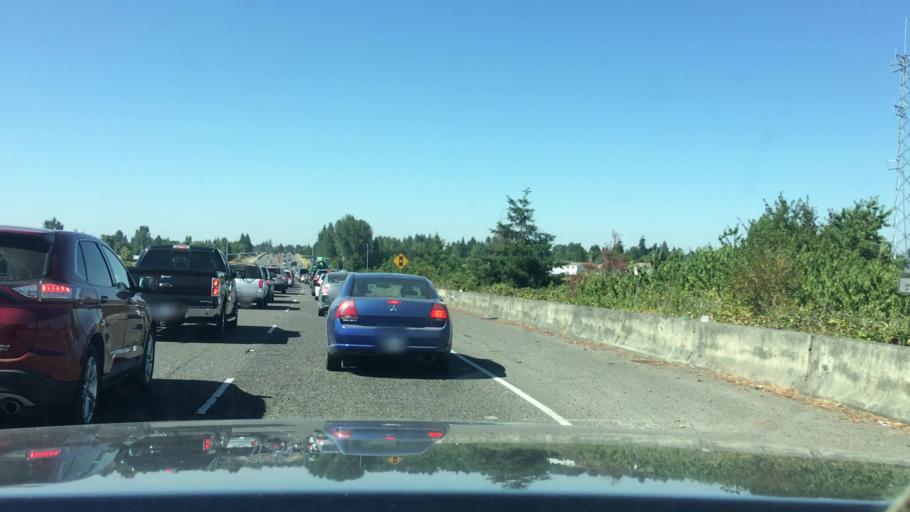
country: US
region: Oregon
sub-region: Lane County
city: Eugene
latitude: 44.0612
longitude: -123.1735
